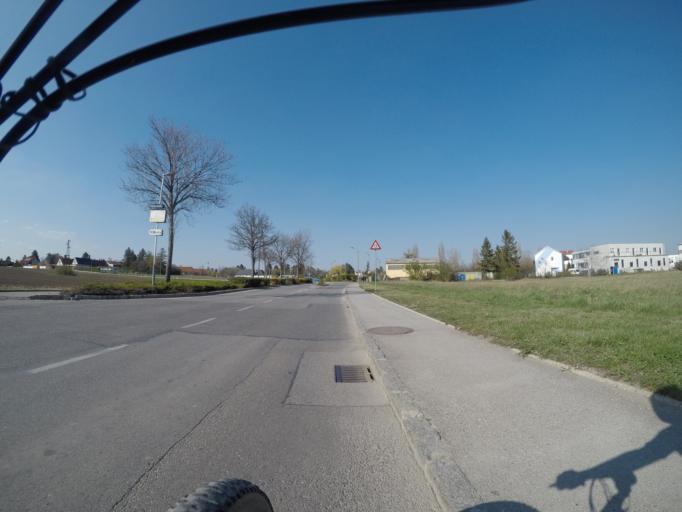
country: AT
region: Lower Austria
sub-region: Politischer Bezirk Modling
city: Neu-Guntramsdorf
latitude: 48.0611
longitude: 16.3232
